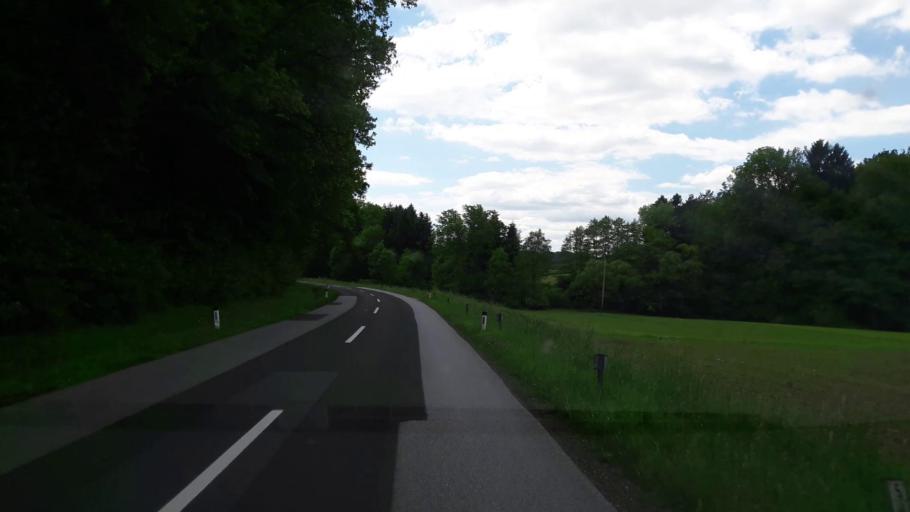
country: AT
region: Styria
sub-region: Politischer Bezirk Hartberg-Fuerstenfeld
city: Soechau
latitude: 47.0369
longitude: 16.0156
